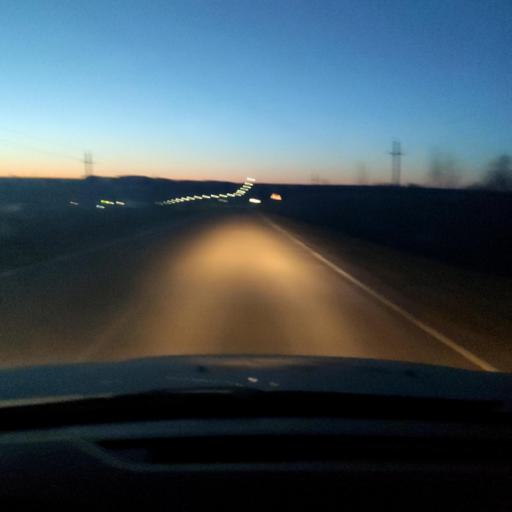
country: RU
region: Bashkortostan
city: Ulukulevo
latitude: 54.5613
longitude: 56.3416
